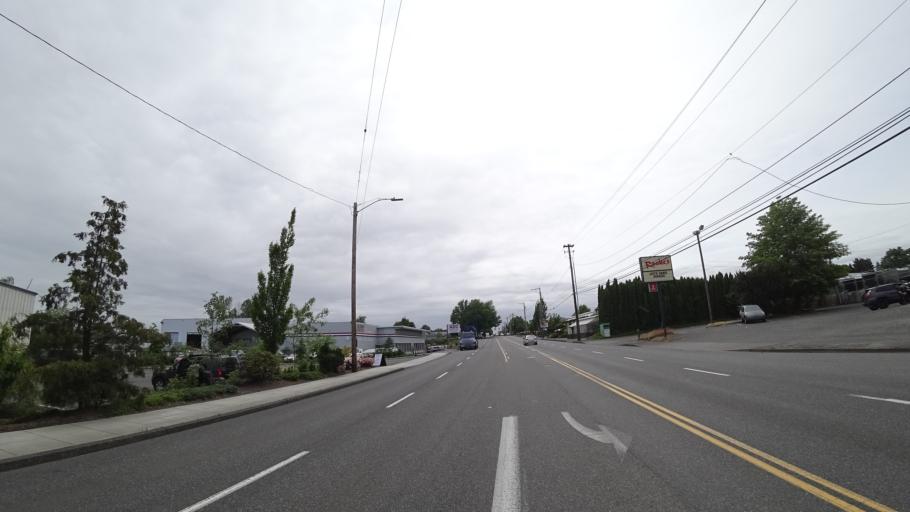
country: US
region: Oregon
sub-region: Multnomah County
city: Portland
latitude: 45.5773
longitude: -122.6472
